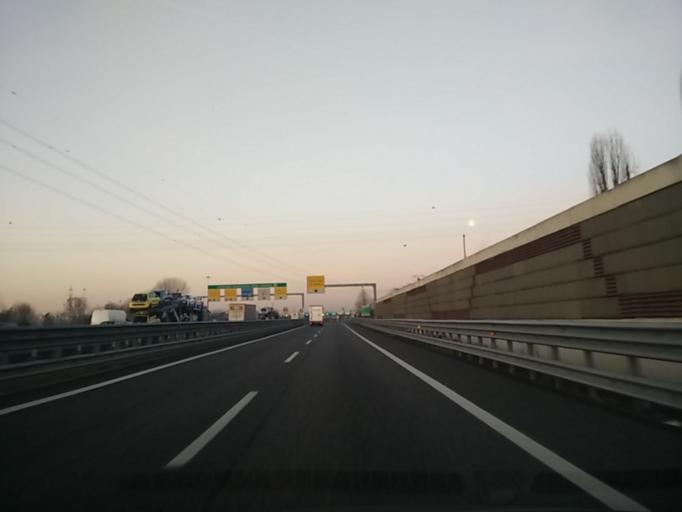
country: IT
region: Lombardy
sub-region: Provincia di Monza e Brianza
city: Monza
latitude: 45.5573
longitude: 9.2742
